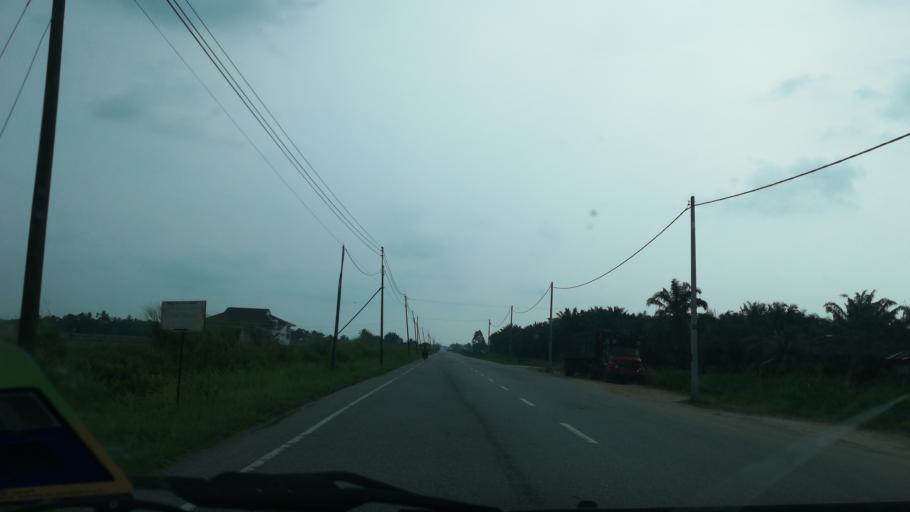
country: MY
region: Perak
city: Teluk Intan
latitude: 4.1100
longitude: 101.0643
